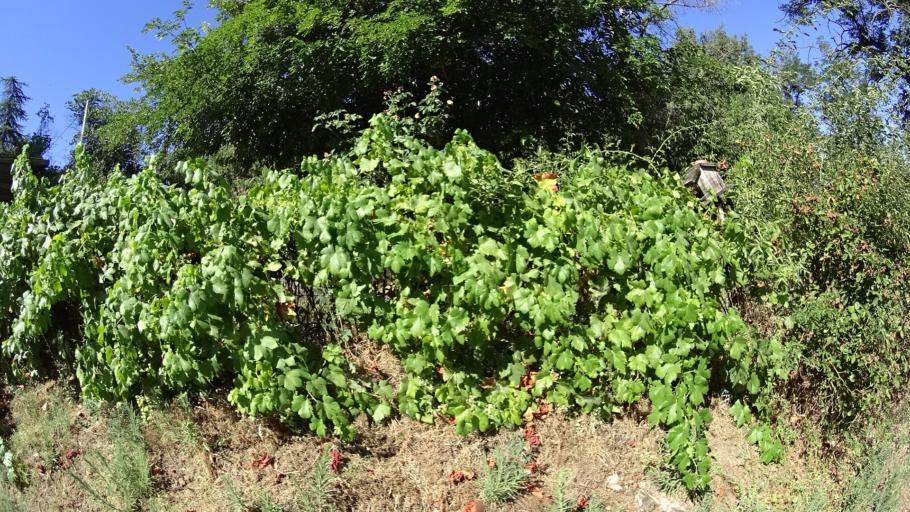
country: US
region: California
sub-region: Calaveras County
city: Murphys
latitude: 38.0839
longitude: -120.4711
